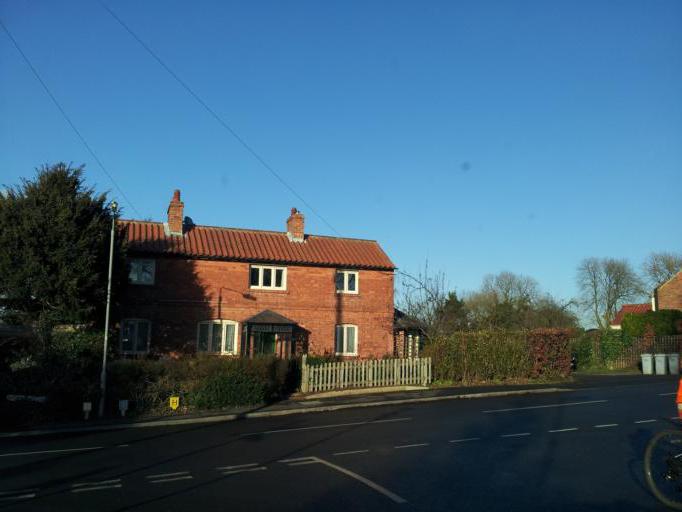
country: GB
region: England
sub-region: Nottinghamshire
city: South Collingham
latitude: 53.0804
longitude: -0.7574
